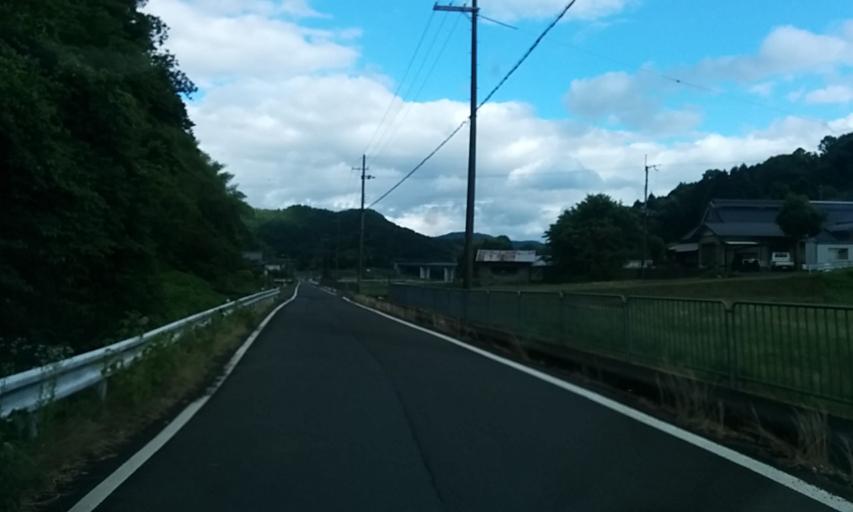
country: JP
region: Kyoto
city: Ayabe
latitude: 35.3519
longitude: 135.2794
